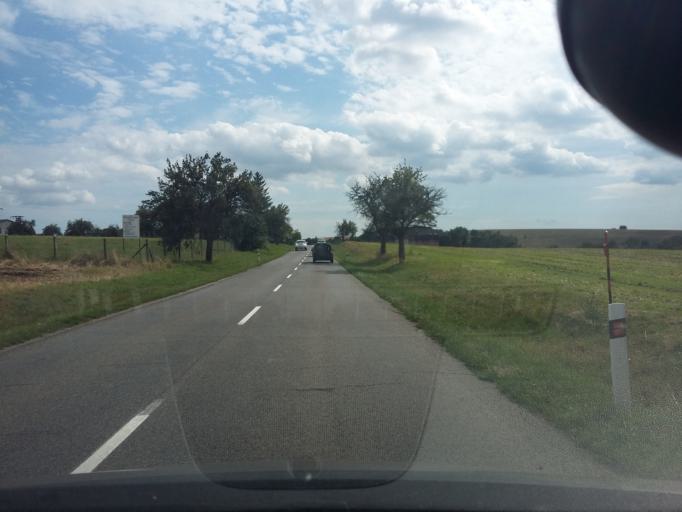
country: SK
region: Trnavsky
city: Gbely
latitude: 48.7282
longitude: 17.1629
